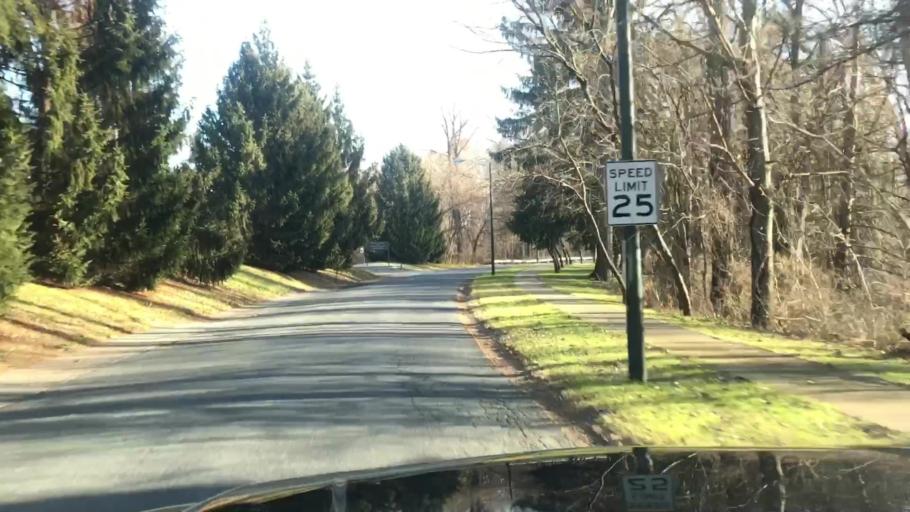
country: US
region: Pennsylvania
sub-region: Dauphin County
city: Harrisburg
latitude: 40.2866
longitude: -76.8769
